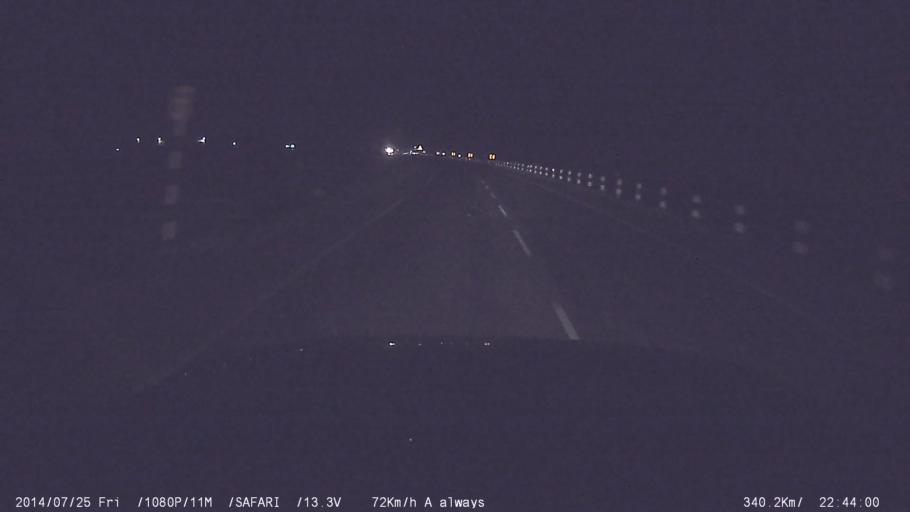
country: IN
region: Tamil Nadu
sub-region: Coimbatore
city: Irugur
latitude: 11.0535
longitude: 77.0810
